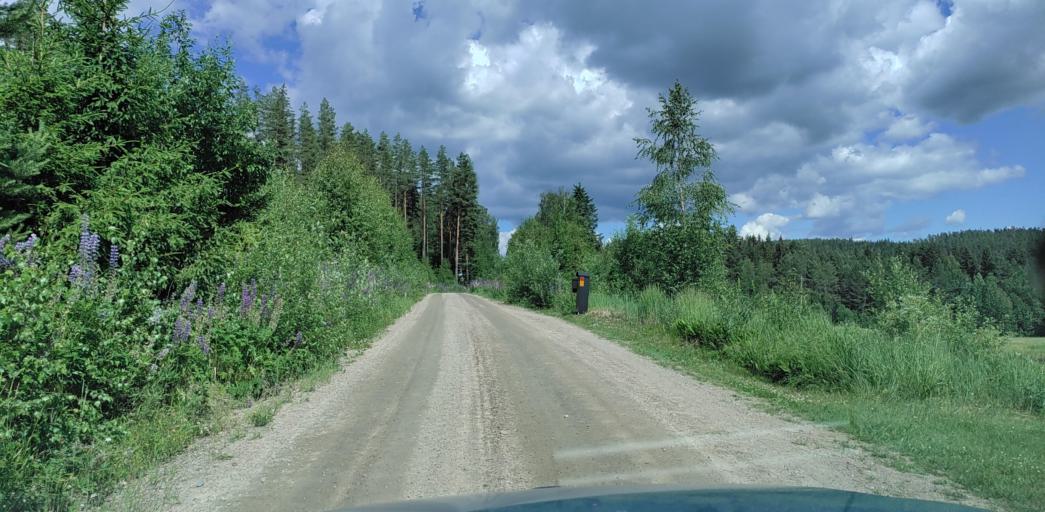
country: SE
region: Vaermland
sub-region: Sunne Kommun
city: Sunne
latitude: 60.0380
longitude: 13.2446
